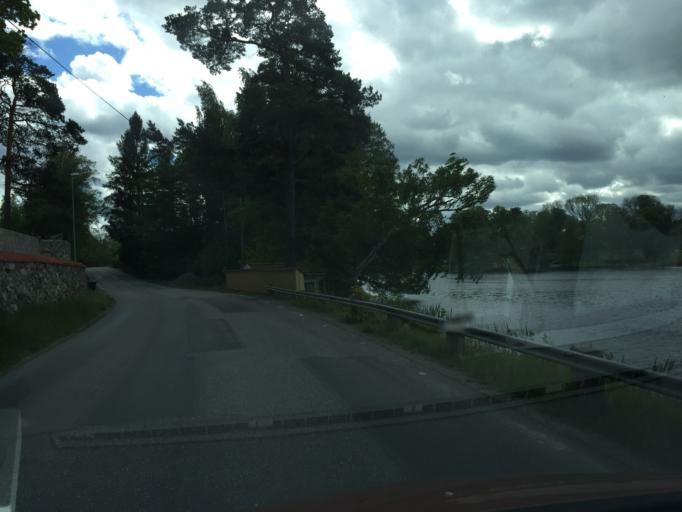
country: SE
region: OEstergoetland
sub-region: Finspangs Kommun
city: Finspang
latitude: 58.7099
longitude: 15.8514
